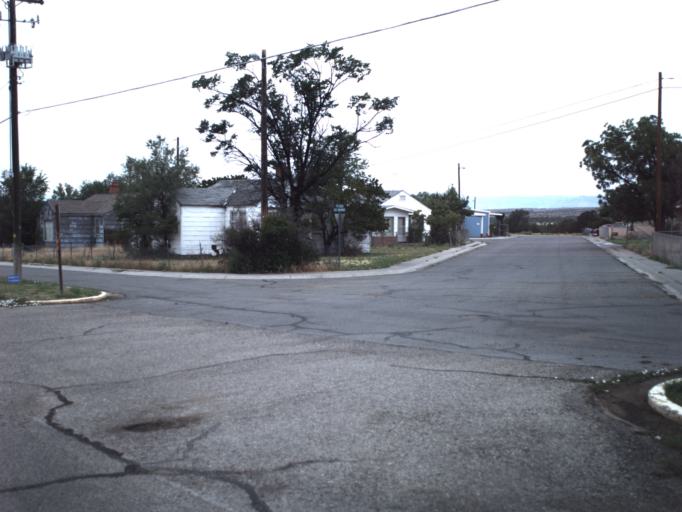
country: US
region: Utah
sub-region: Carbon County
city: East Carbon City
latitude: 39.5431
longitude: -110.4152
